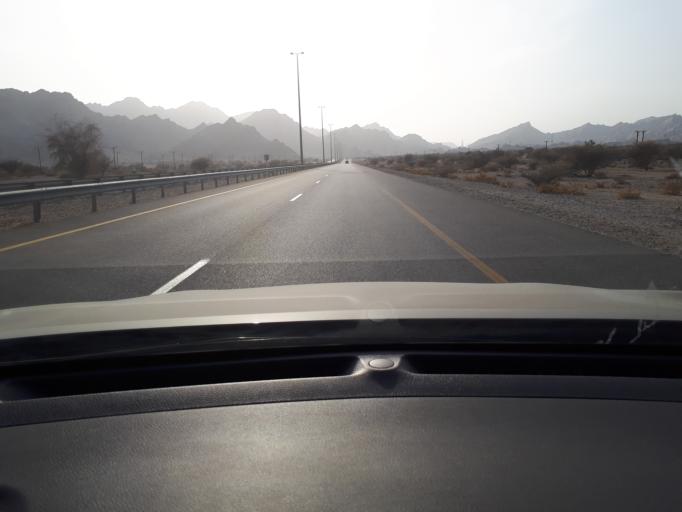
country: OM
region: Muhafazat Masqat
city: Muscat
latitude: 23.3645
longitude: 58.6588
